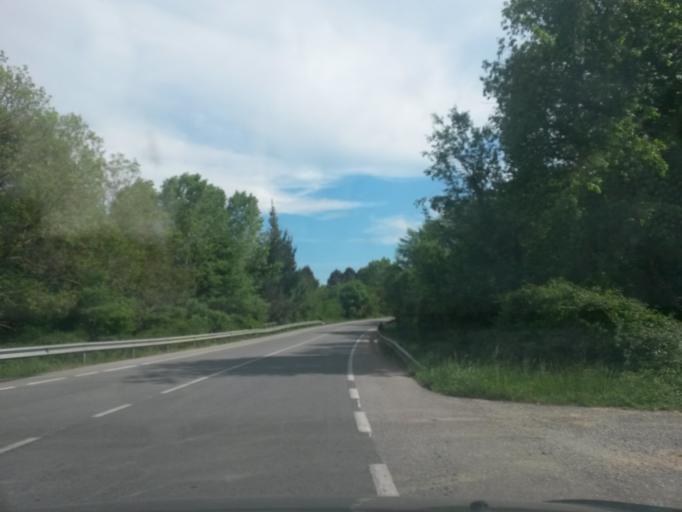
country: ES
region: Catalonia
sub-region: Provincia de Girona
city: Brunyola
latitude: 41.9064
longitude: 2.6623
